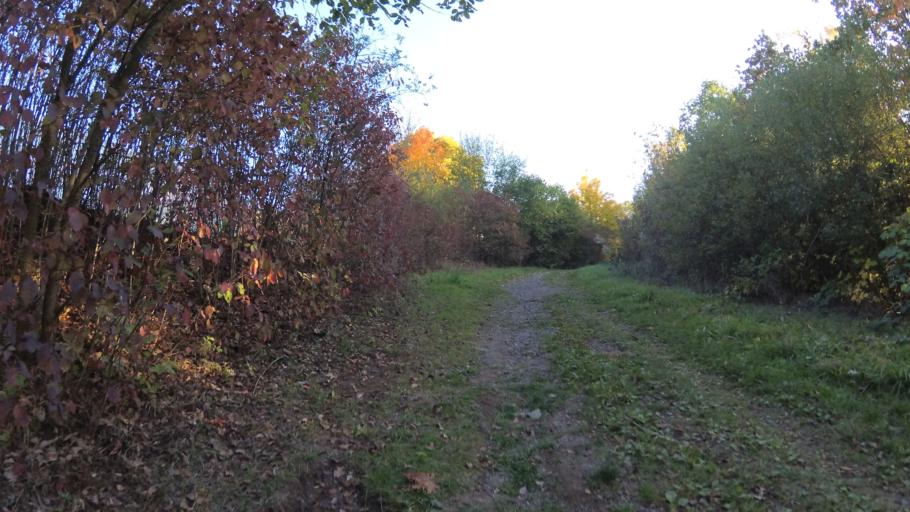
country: DE
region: Saarland
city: Sankt Wendel
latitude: 49.4578
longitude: 7.1820
